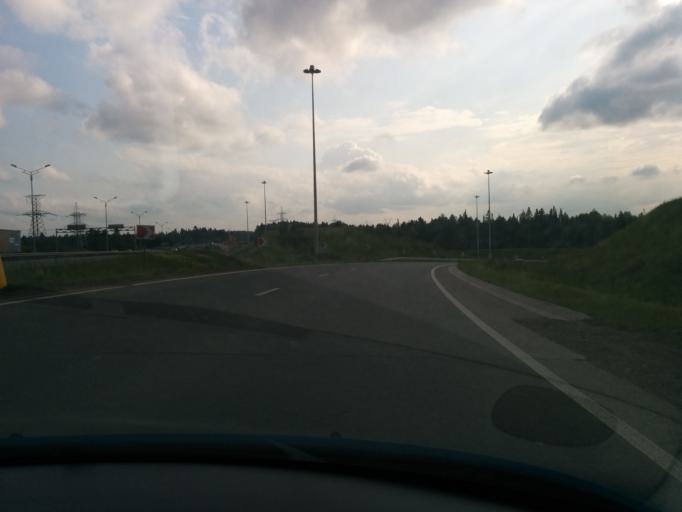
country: RU
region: Perm
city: Ferma
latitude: 58.0000
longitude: 56.3874
